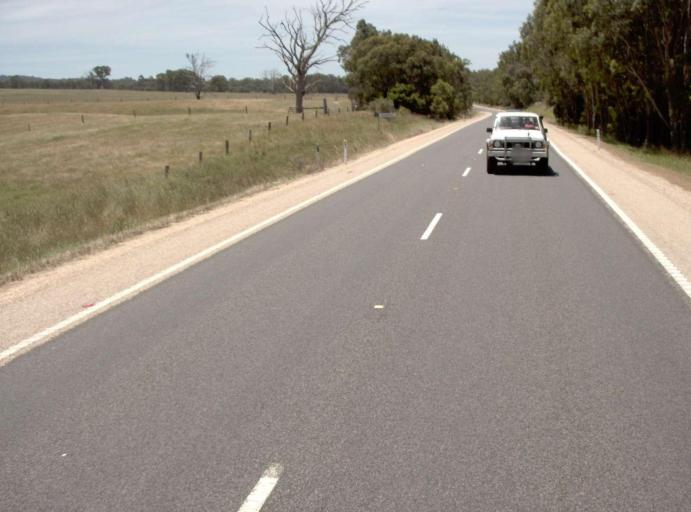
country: AU
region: Victoria
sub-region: East Gippsland
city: Bairnsdale
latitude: -37.7586
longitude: 147.7076
